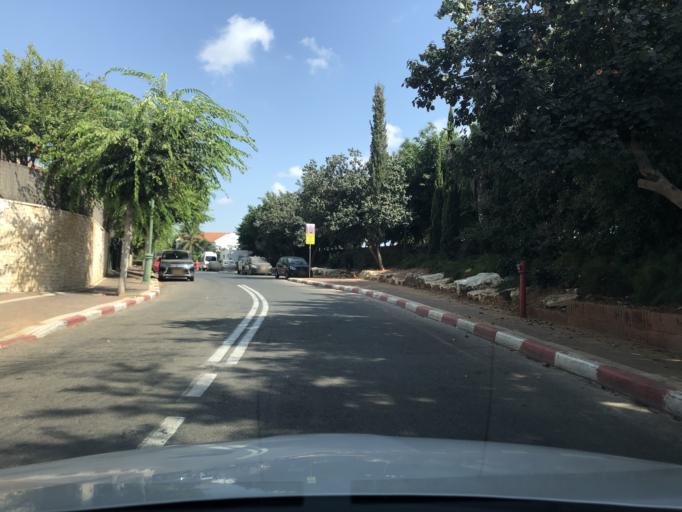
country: IL
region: Tel Aviv
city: Giv`at Shemu'el
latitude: 32.0627
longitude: 34.8463
